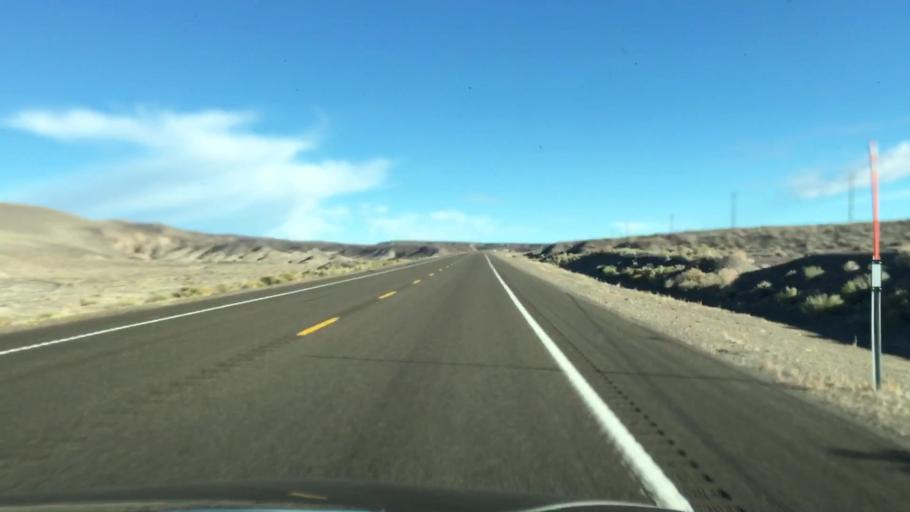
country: US
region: Nevada
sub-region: Mineral County
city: Hawthorne
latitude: 38.2376
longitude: -118.0319
